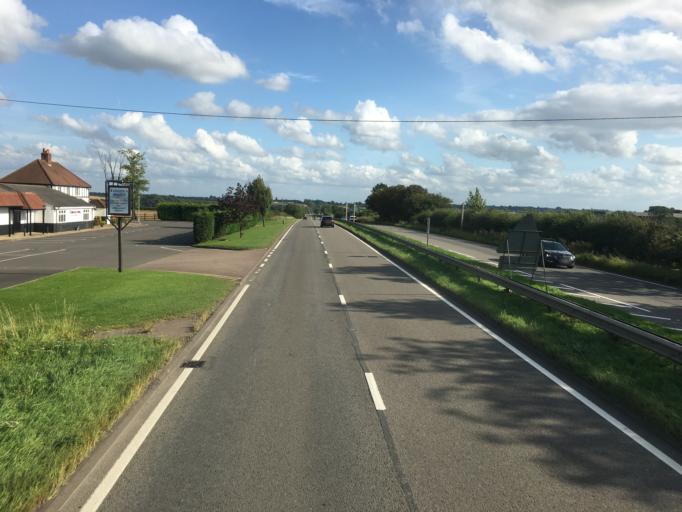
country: GB
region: England
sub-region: Leicestershire
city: Lutterworth
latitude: 52.4452
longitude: -1.2473
